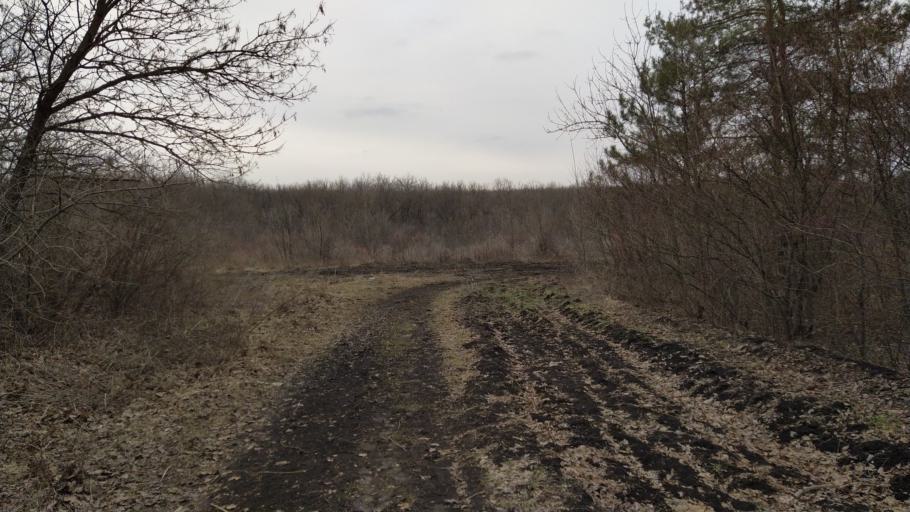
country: RU
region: Rostov
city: Temernik
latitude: 47.3497
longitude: 39.7472
